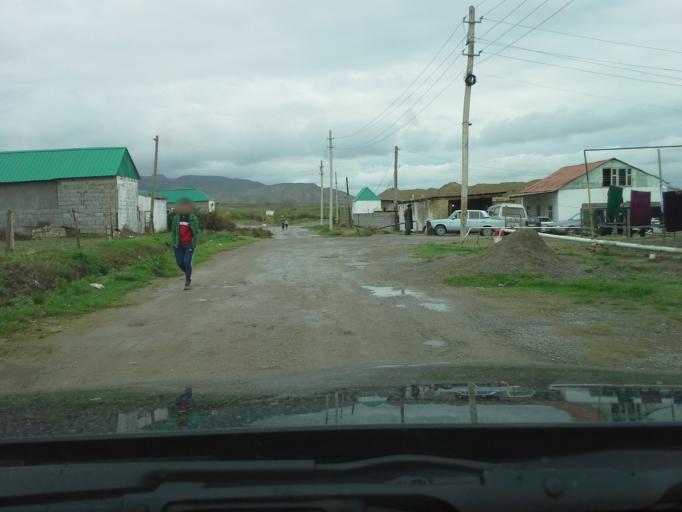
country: TM
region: Ahal
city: Abadan
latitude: 37.9612
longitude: 58.2011
